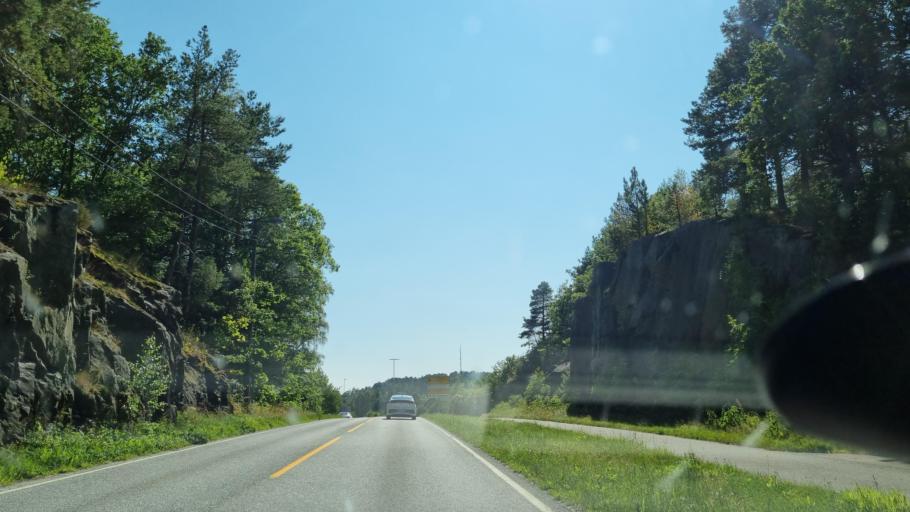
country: NO
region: Aust-Agder
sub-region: Arendal
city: Arendal
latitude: 58.4653
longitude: 8.8229
